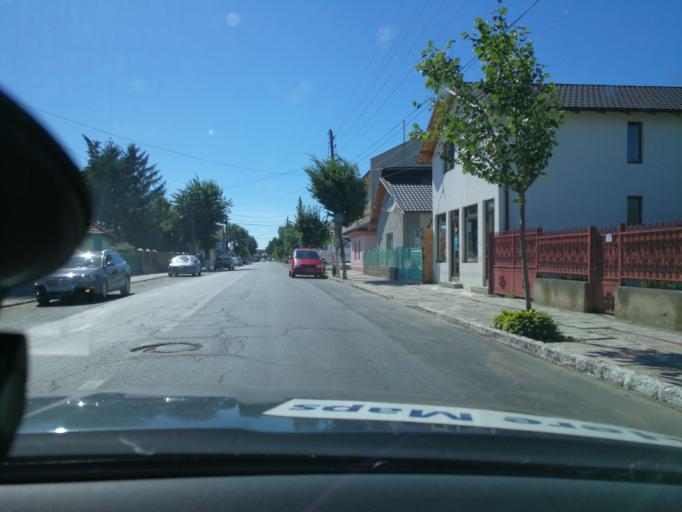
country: RO
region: Tulcea
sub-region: Oras Macin
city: Macin
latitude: 45.2429
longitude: 28.1403
